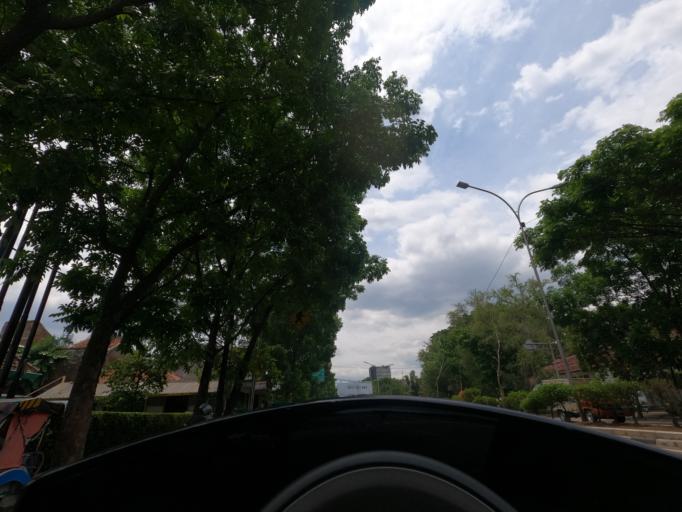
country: ID
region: West Java
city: Bandung
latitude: -6.9177
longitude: 107.6309
